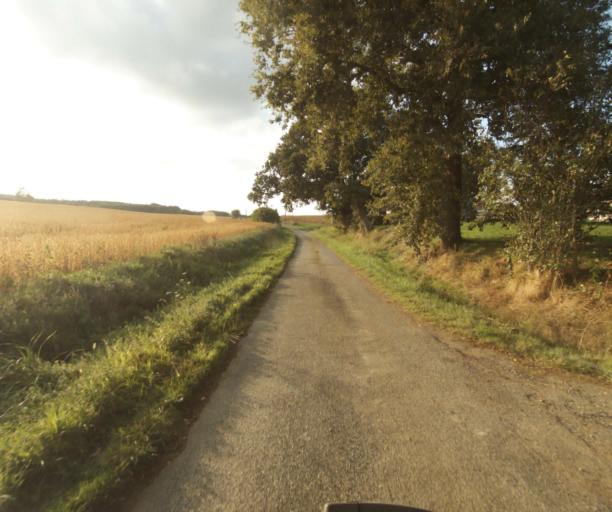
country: FR
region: Midi-Pyrenees
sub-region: Departement de la Haute-Garonne
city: Launac
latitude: 43.8309
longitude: 1.1328
